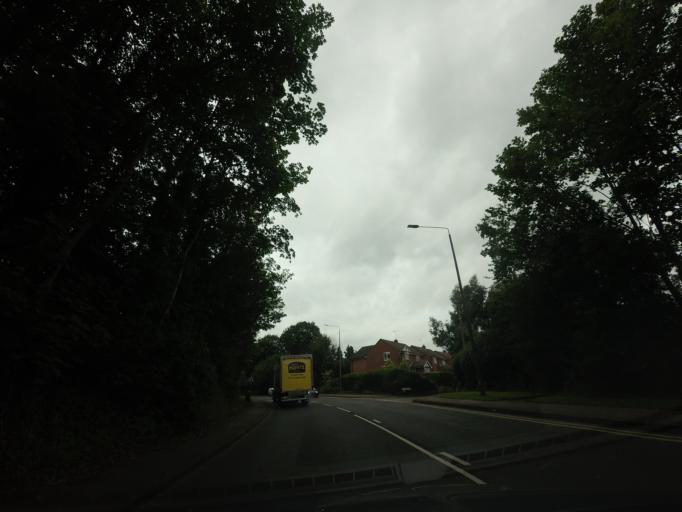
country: GB
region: England
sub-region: Nottinghamshire
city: Kimberley
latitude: 52.9969
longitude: -1.2352
